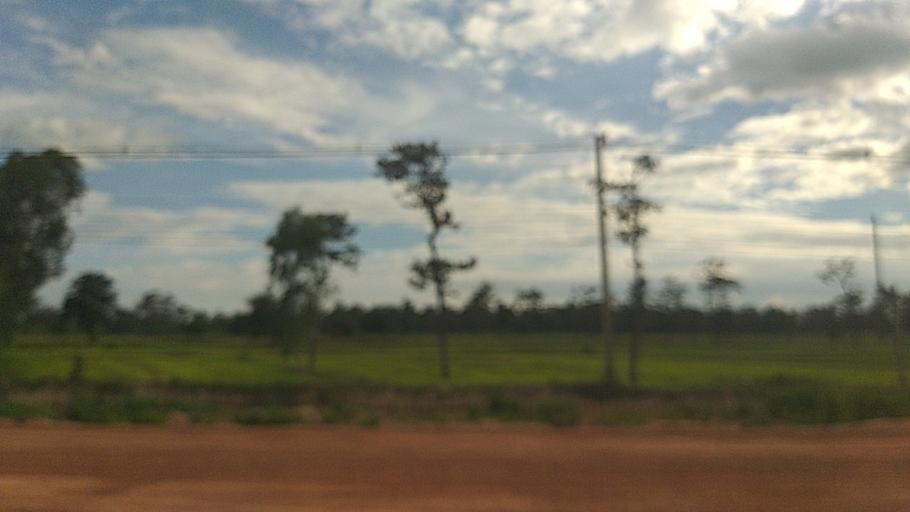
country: TH
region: Surin
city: Kap Choeng
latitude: 14.5160
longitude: 103.5466
